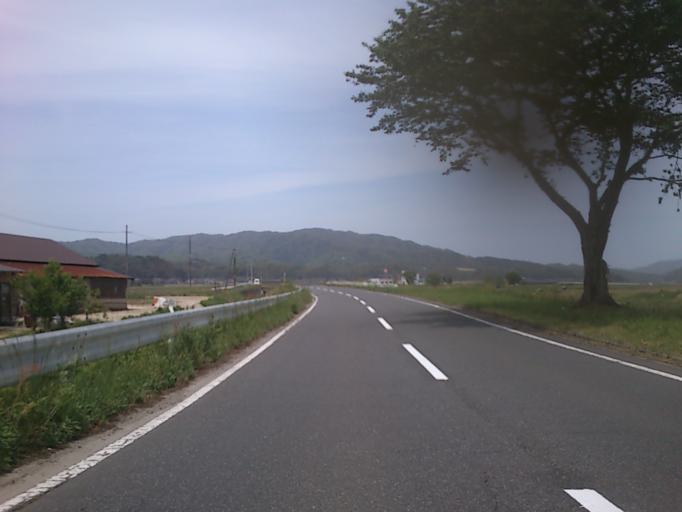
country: JP
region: Kyoto
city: Miyazu
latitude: 35.6627
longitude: 135.0865
